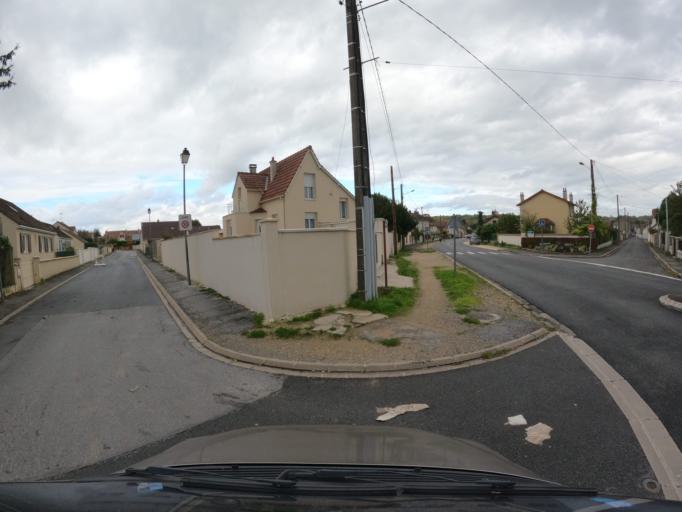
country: FR
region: Ile-de-France
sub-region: Departement de Seine-et-Marne
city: Saint-Germain-sur-Morin
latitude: 48.8789
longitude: 2.8511
